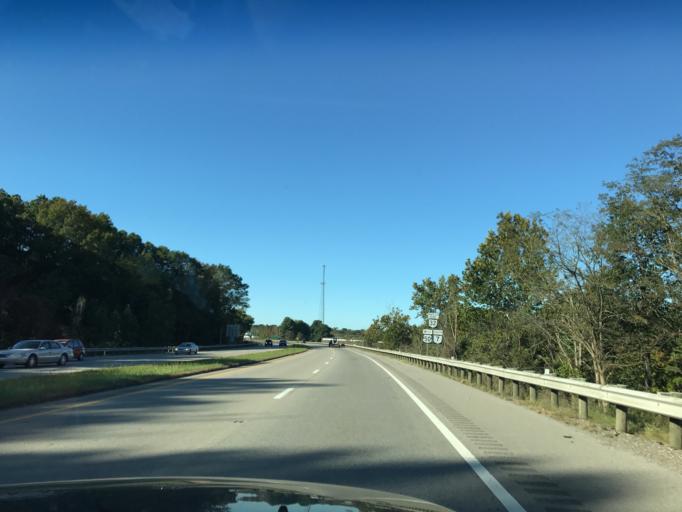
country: US
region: West Virginia
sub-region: Wood County
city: Washington
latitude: 39.2818
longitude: -81.6820
